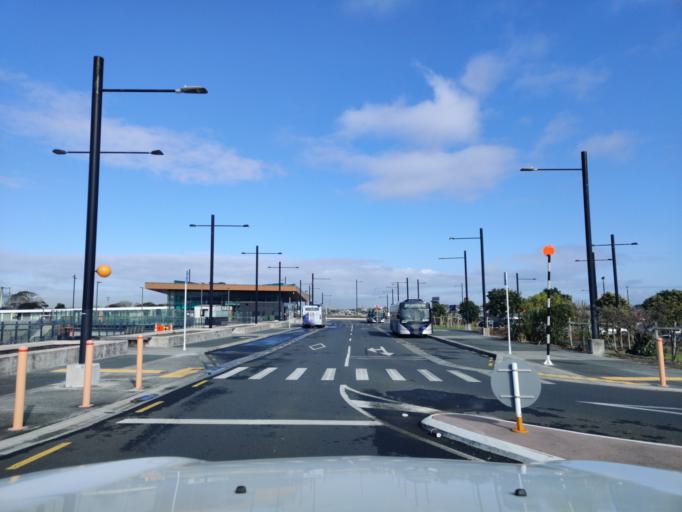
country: NZ
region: Auckland
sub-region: Auckland
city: Tamaki
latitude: -36.8971
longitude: 174.8500
